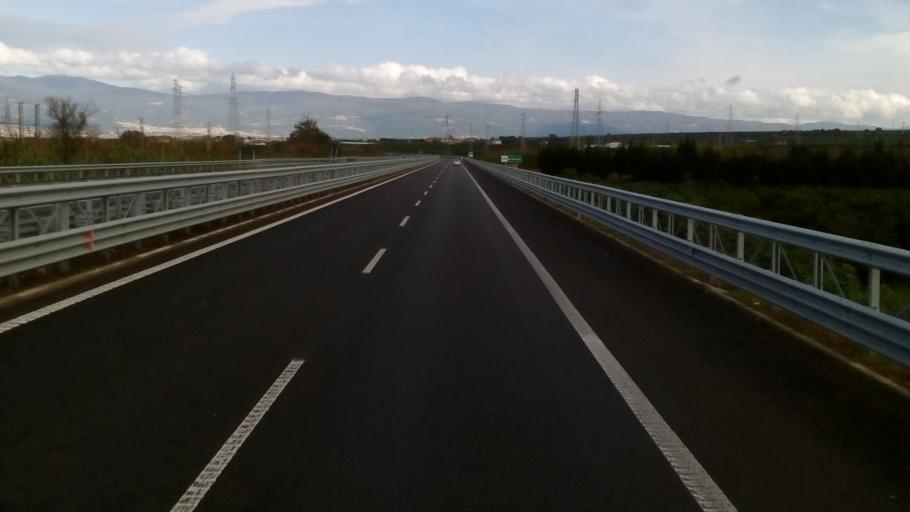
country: IT
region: Calabria
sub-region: Provincia di Catanzaro
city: Acconia
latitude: 38.8524
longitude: 16.2706
